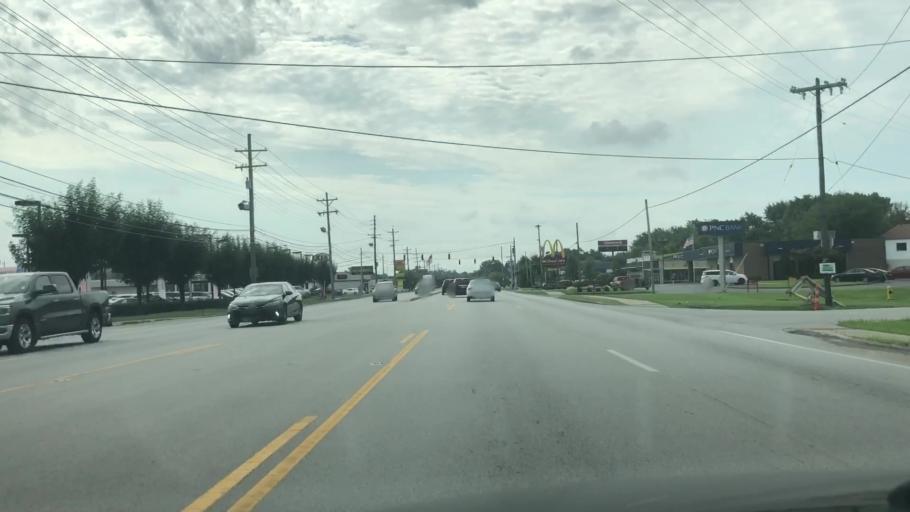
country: US
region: Kentucky
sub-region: Jefferson County
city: Okolona
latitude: 38.1698
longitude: -85.7078
